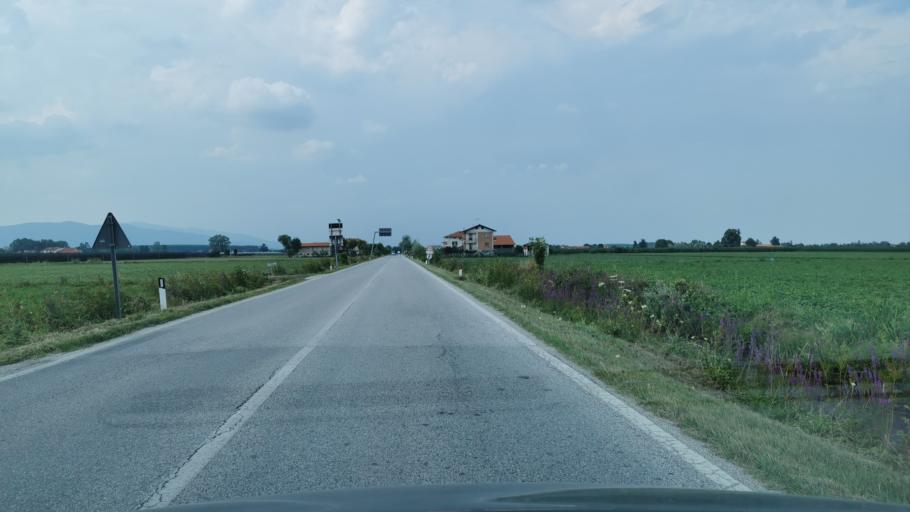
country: IT
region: Piedmont
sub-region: Provincia di Cuneo
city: Roata Rossi
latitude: 44.4405
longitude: 7.5432
